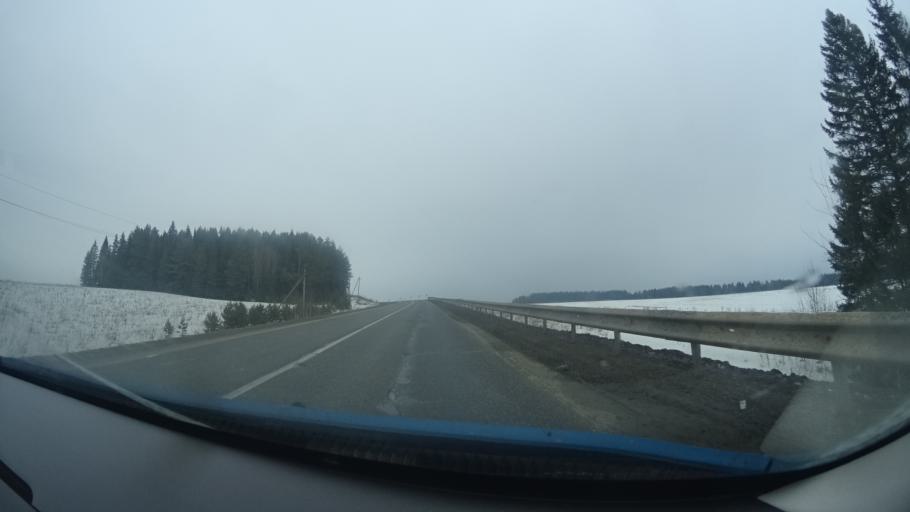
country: RU
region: Perm
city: Osa
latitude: 57.3130
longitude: 55.6219
